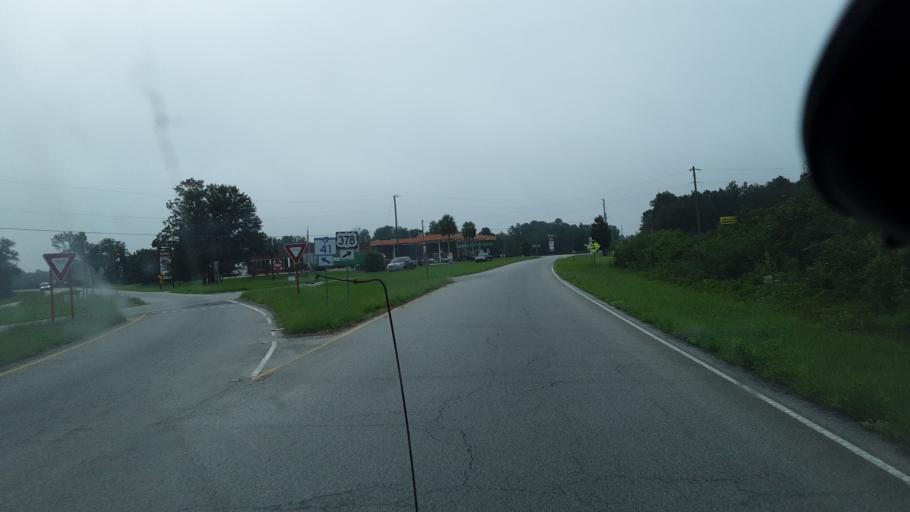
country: US
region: South Carolina
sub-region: Florence County
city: Johnsonville
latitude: 33.9127
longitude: -79.4083
